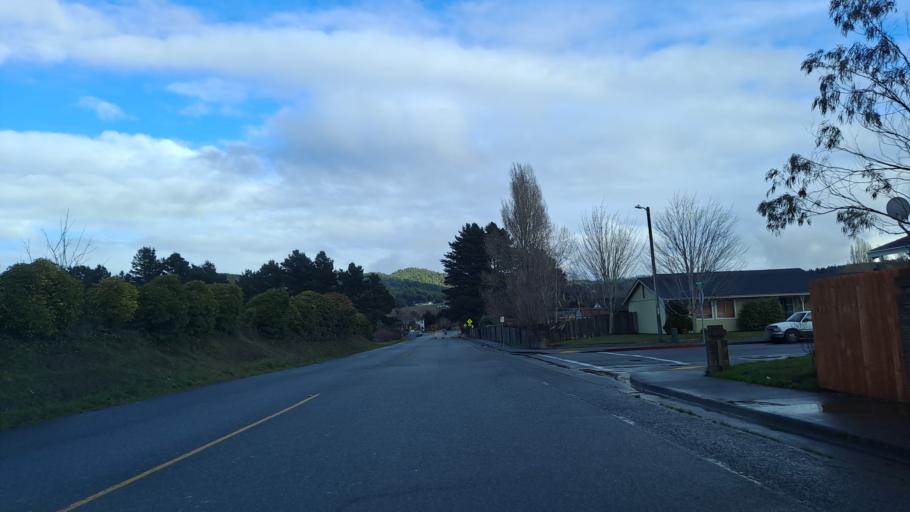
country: US
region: California
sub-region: Humboldt County
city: Fortuna
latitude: 40.5847
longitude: -124.1433
